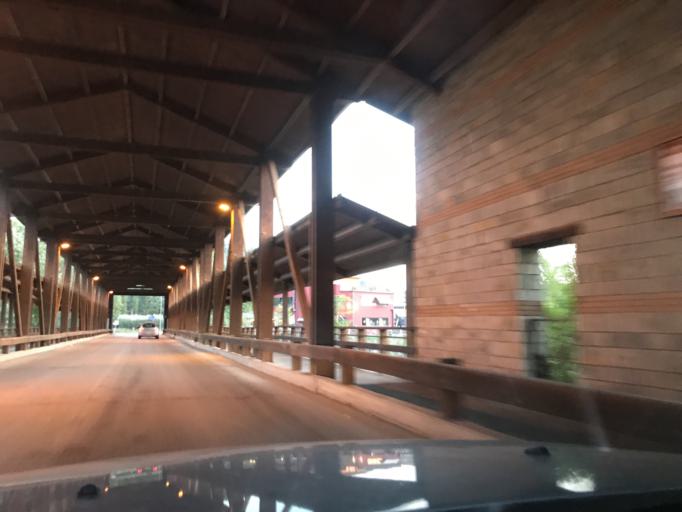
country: IT
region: Umbria
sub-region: Provincia di Perugia
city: Via Lippia
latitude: 43.0912
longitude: 12.4499
